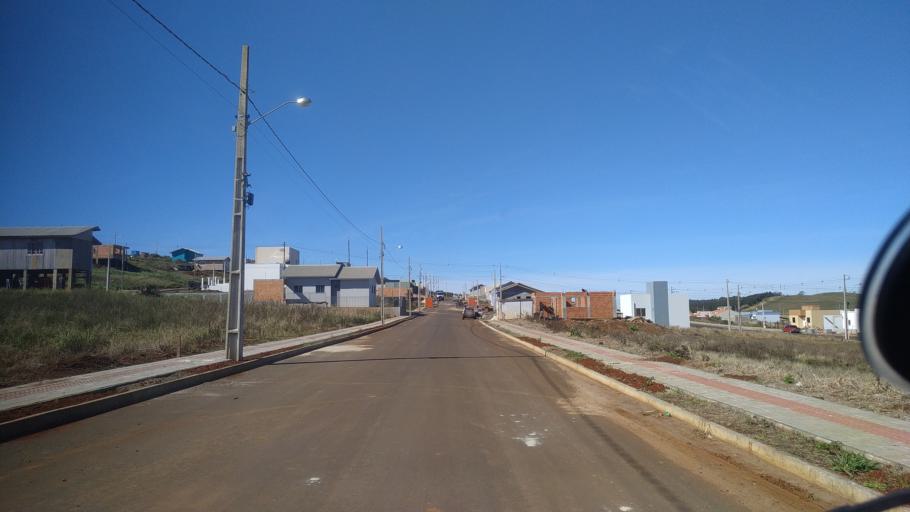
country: BR
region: Santa Catarina
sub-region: Chapeco
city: Chapeco
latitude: -27.0514
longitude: -52.5964
